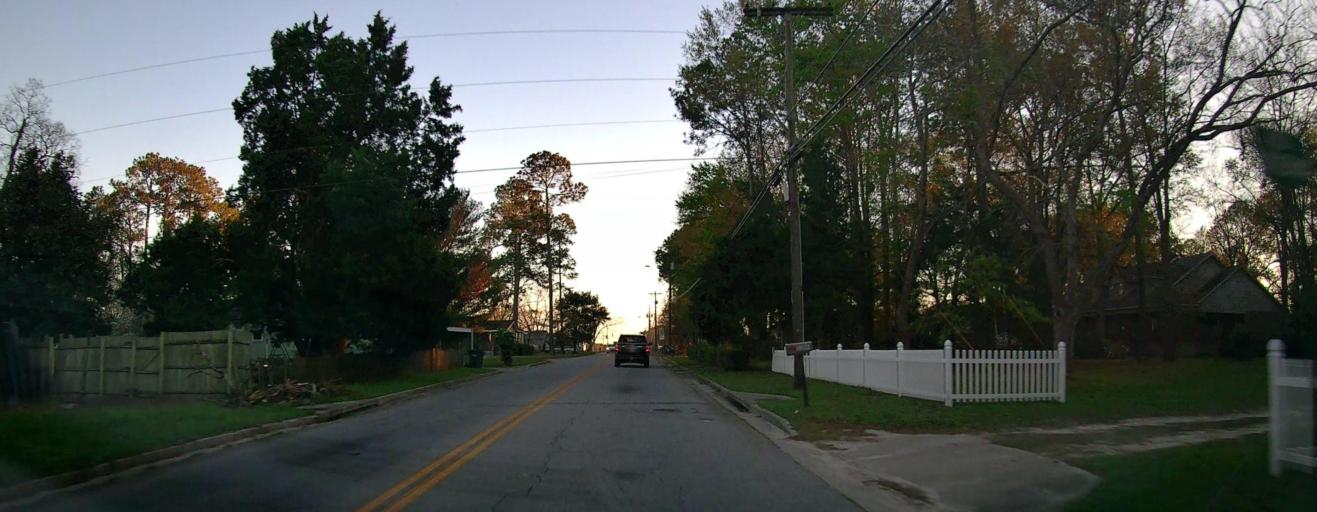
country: US
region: Georgia
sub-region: Crisp County
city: Cordele
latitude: 31.9571
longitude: -83.7655
